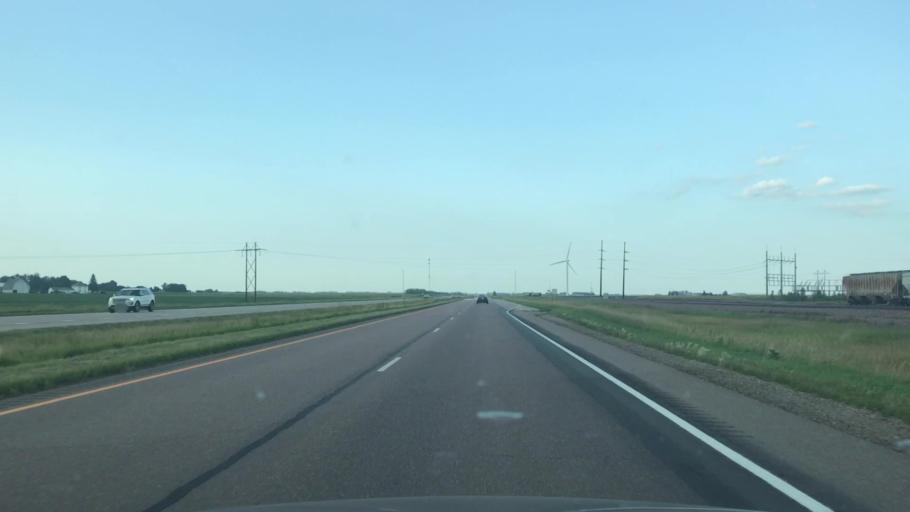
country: US
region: Minnesota
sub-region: Nobles County
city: Worthington
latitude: 43.7081
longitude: -95.4569
